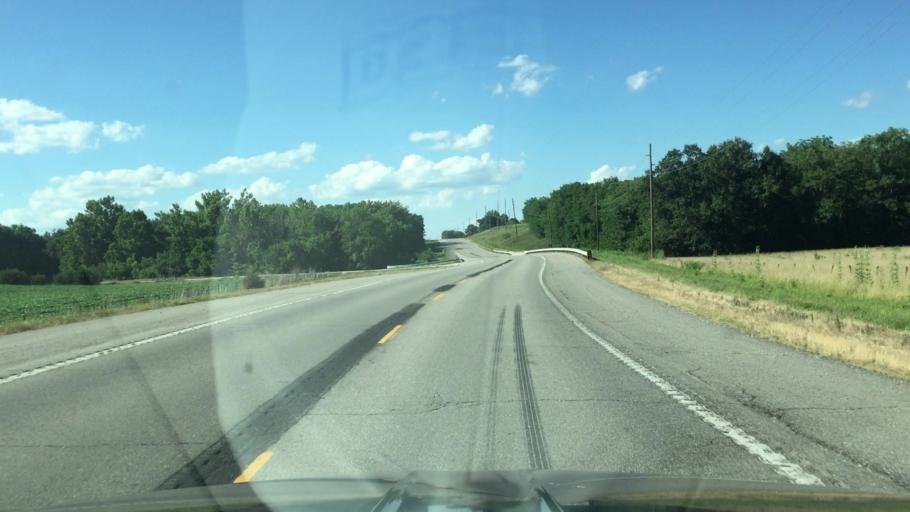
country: US
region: Missouri
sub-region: Moniteau County
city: Tipton
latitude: 38.6291
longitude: -92.7894
